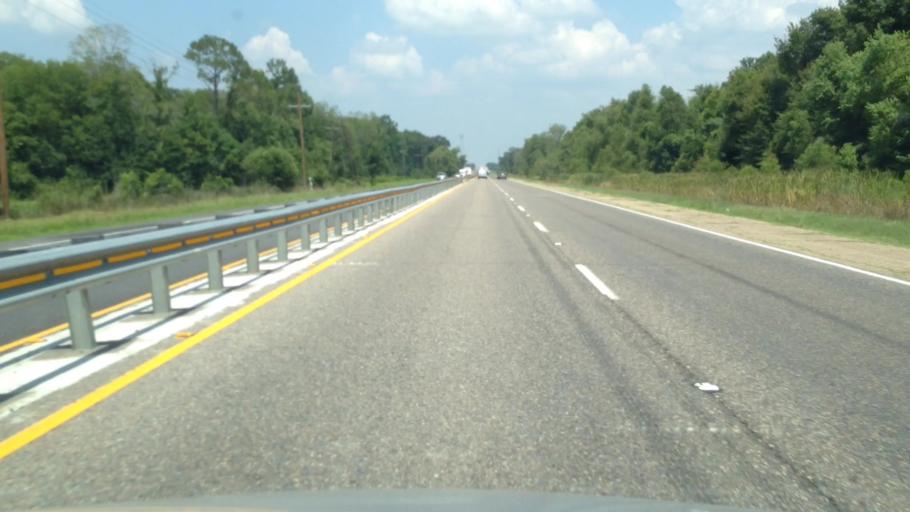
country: US
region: Louisiana
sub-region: Pointe Coupee Parish
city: Livonia
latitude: 30.5556
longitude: -91.5949
